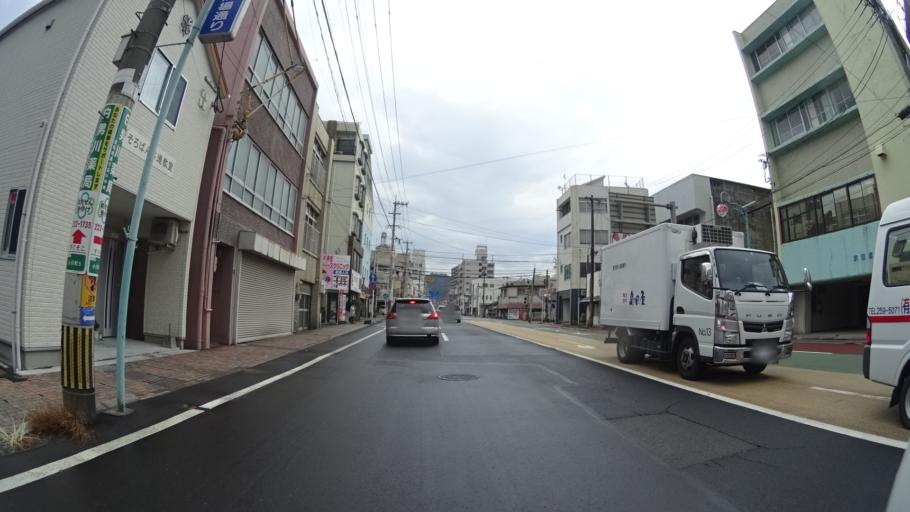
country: JP
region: Kagoshima
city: Kagoshima-shi
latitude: 31.6007
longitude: 130.5606
